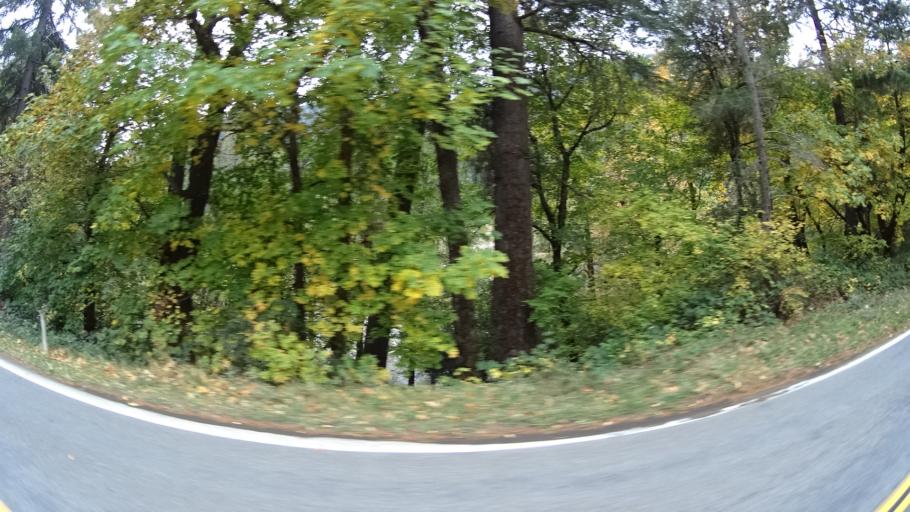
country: US
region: California
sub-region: Siskiyou County
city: Happy Camp
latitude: 41.8420
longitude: -123.3834
